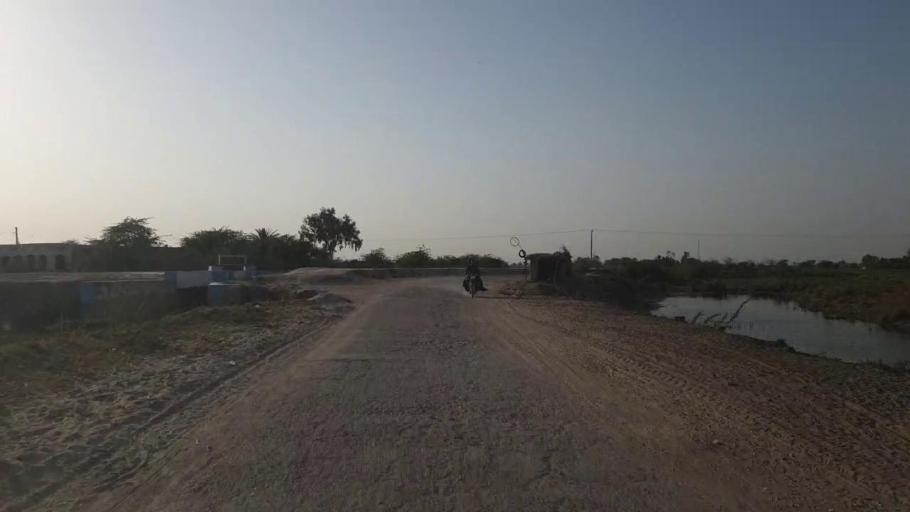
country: PK
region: Sindh
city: Dhoro Naro
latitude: 25.4889
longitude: 69.5687
